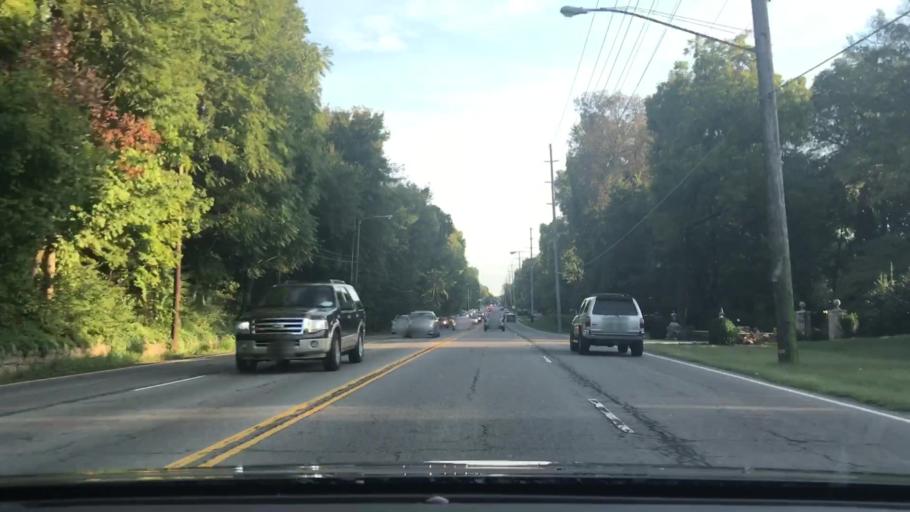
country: US
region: Tennessee
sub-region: Davidson County
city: Oak Hill
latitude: 36.1024
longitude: -86.7725
